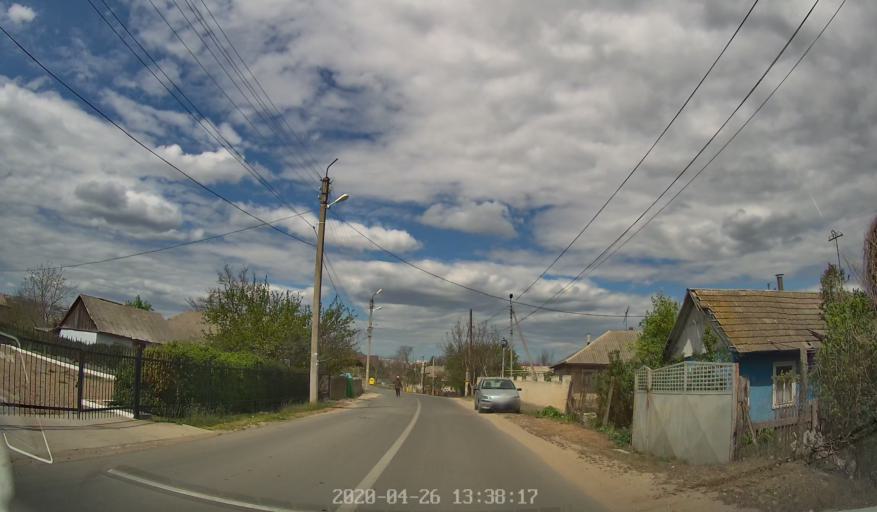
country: MD
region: Criuleni
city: Criuleni
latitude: 47.2071
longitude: 29.1672
